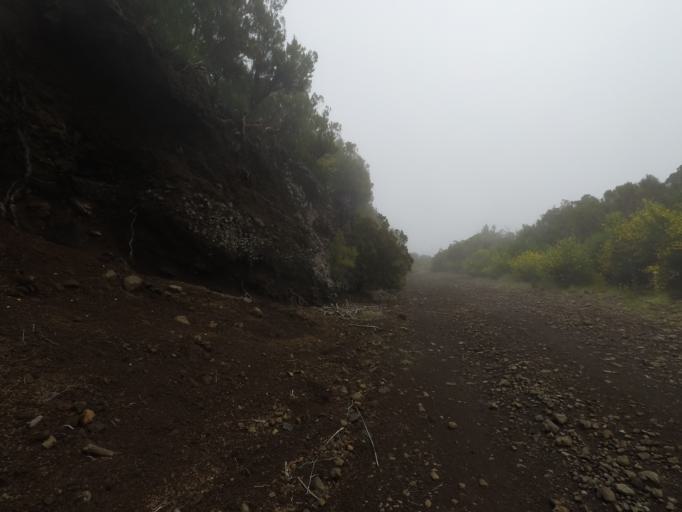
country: PT
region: Madeira
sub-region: Sao Vicente
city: Sao Vicente
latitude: 32.7734
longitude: -17.0660
